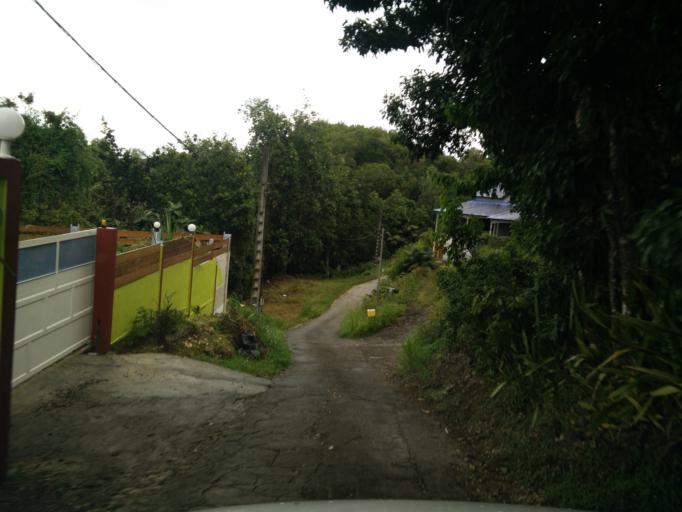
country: GP
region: Guadeloupe
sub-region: Guadeloupe
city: Le Gosier
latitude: 16.2335
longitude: -61.4937
